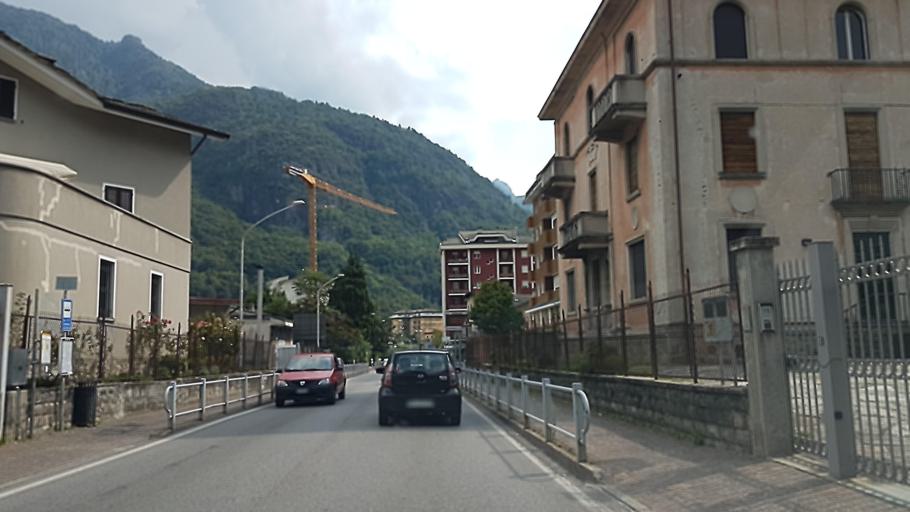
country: IT
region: Lombardy
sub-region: Provincia di Sondrio
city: Chiavenna
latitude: 46.3204
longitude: 9.3981
